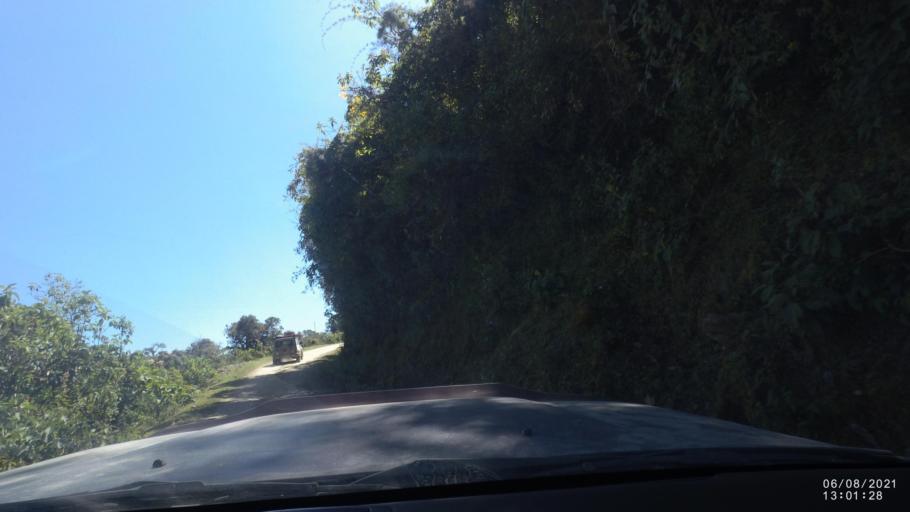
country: BO
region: Cochabamba
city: Colchani
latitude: -16.7440
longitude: -66.6909
